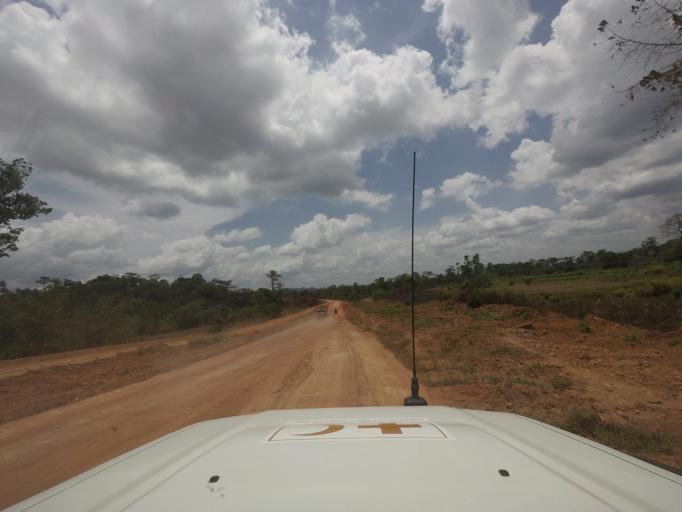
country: LR
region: Nimba
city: Sanniquellie
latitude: 7.2648
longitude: -8.8470
